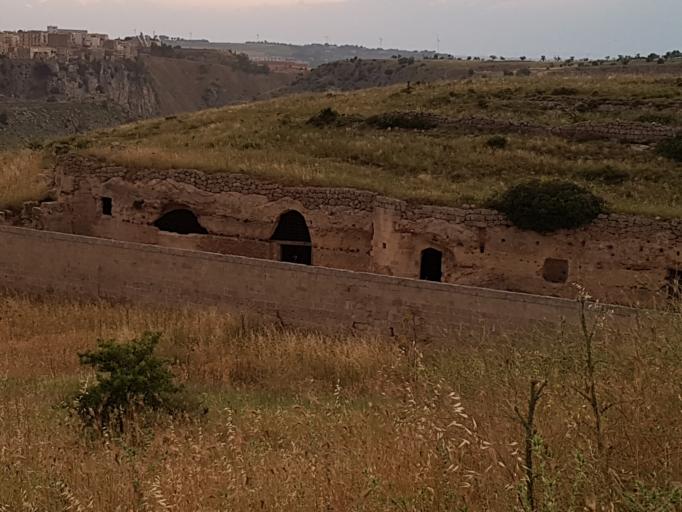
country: IT
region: Basilicate
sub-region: Provincia di Matera
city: Matera
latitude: 40.6669
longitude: 16.6214
